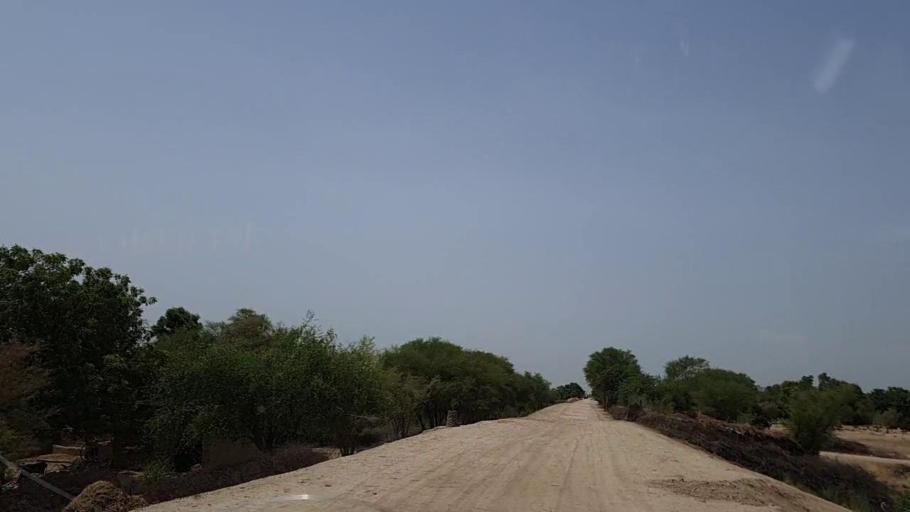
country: PK
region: Sindh
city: Tharu Shah
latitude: 27.0333
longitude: 68.1124
